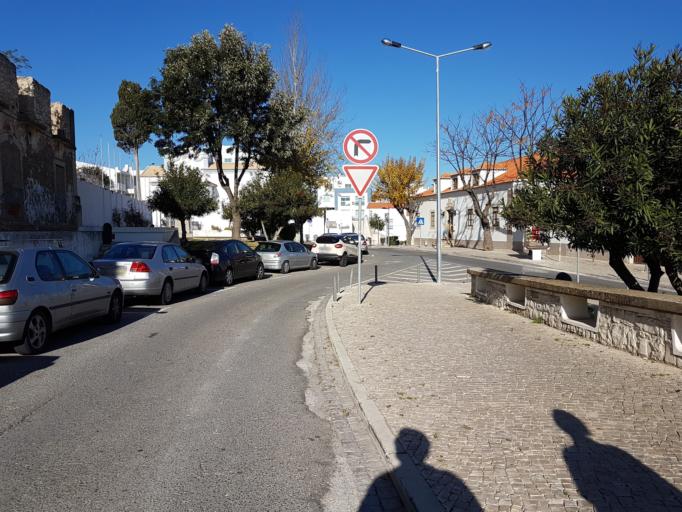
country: PT
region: Faro
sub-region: Albufeira
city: Albufeira
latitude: 37.0871
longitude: -8.2555
